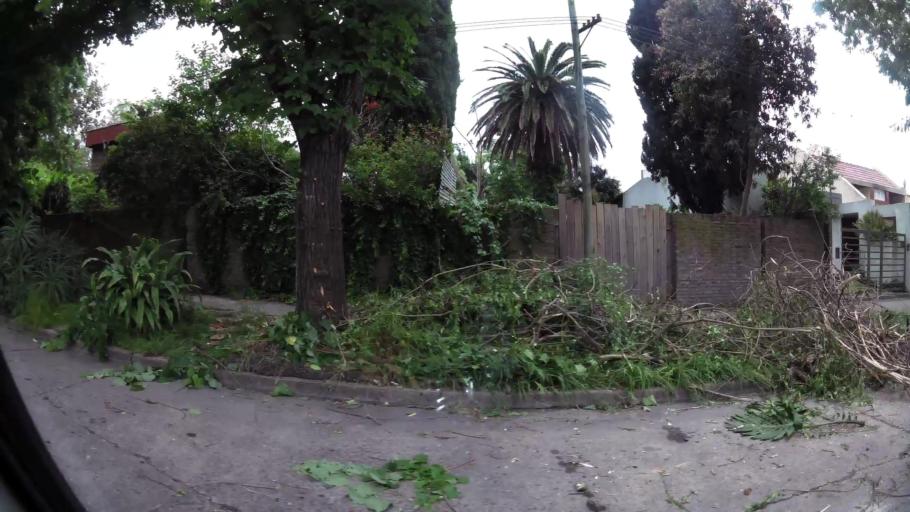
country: AR
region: Buenos Aires
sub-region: Partido de La Plata
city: La Plata
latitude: -34.9398
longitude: -57.9681
